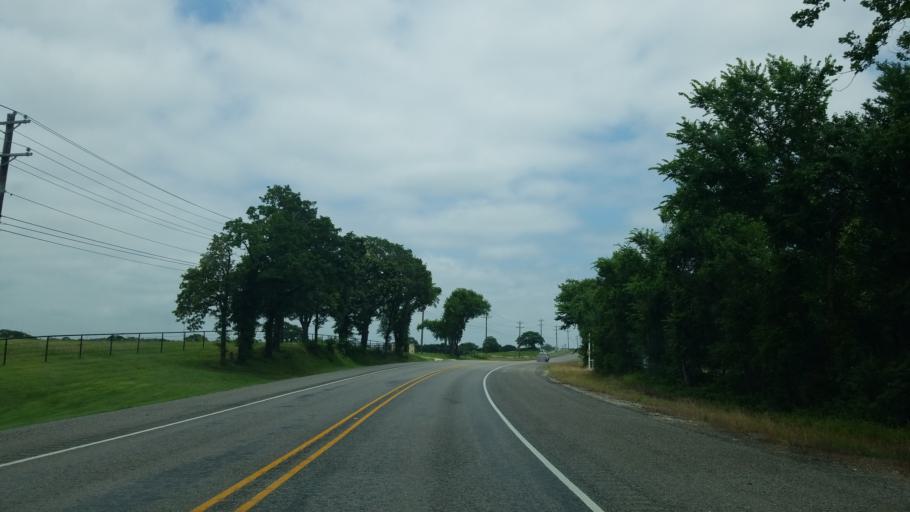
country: US
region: Texas
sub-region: Denton County
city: Aubrey
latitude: 33.3045
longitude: -97.0104
